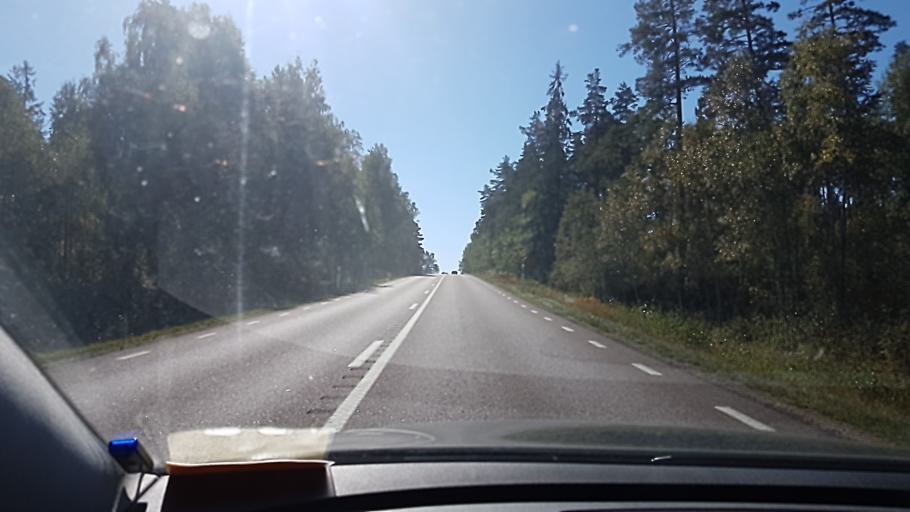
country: SE
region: Kronoberg
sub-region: Lessebo Kommun
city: Lessebo
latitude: 56.7660
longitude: 15.2633
